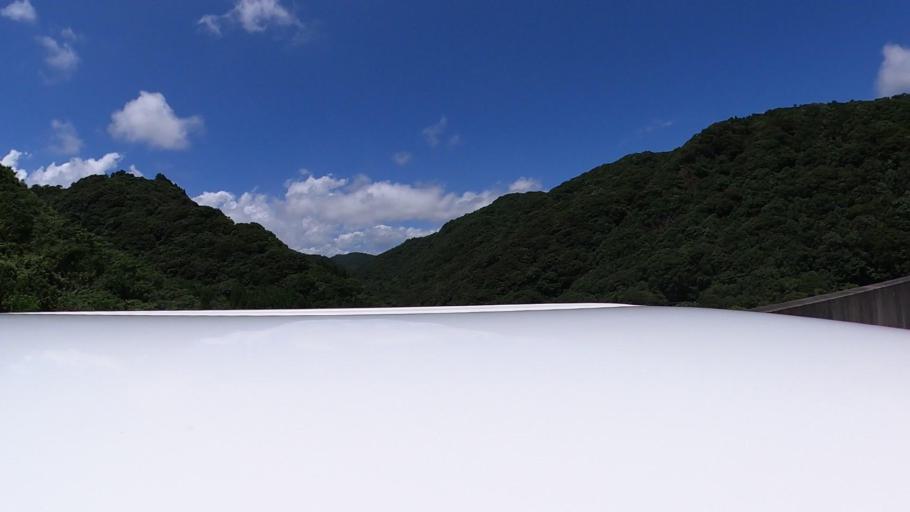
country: JP
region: Miyazaki
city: Takanabe
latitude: 32.3320
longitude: 131.5873
